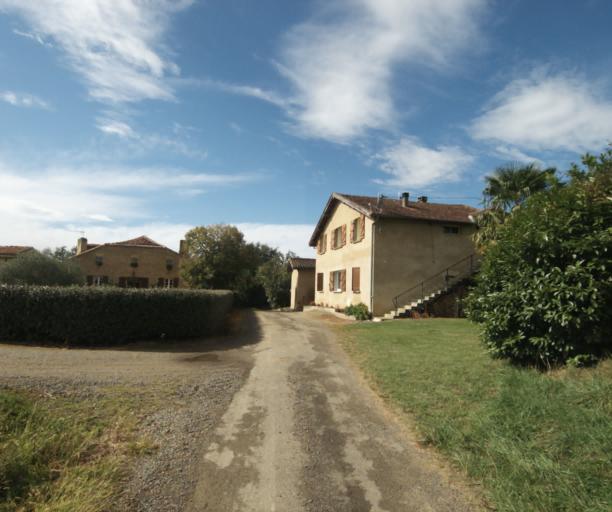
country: FR
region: Midi-Pyrenees
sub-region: Departement du Gers
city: Cazaubon
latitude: 43.8984
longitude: -0.1849
